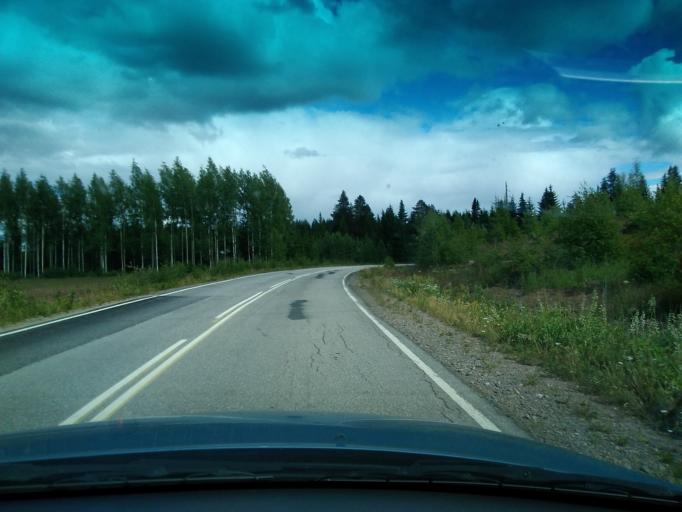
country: FI
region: Central Finland
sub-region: Saarijaervi-Viitasaari
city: Saarijaervi
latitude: 62.7338
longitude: 25.1477
